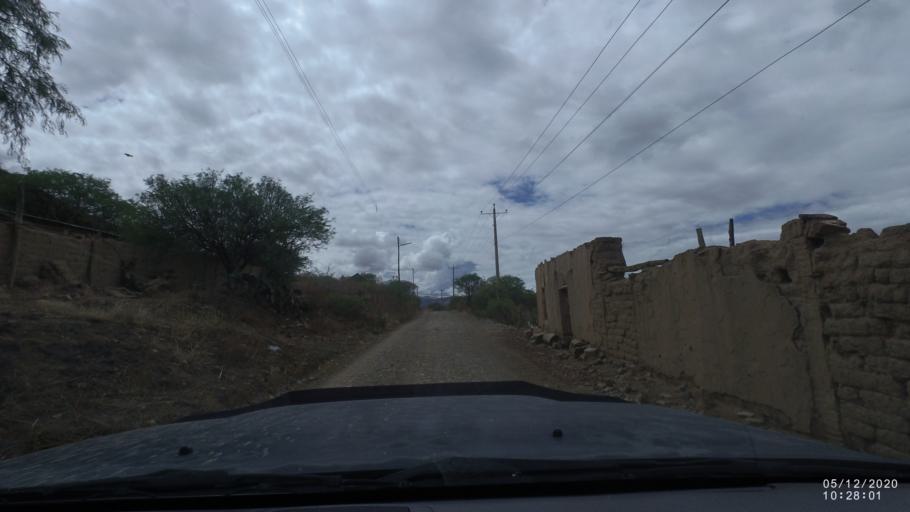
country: BO
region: Cochabamba
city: Sipe Sipe
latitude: -17.5357
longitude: -66.2760
